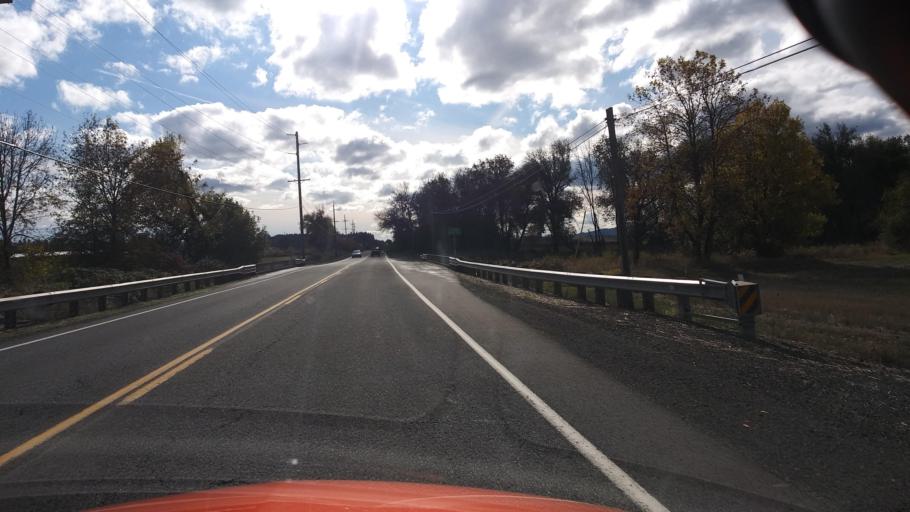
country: US
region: Oregon
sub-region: Washington County
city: Banks
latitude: 45.5743
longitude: -123.1094
